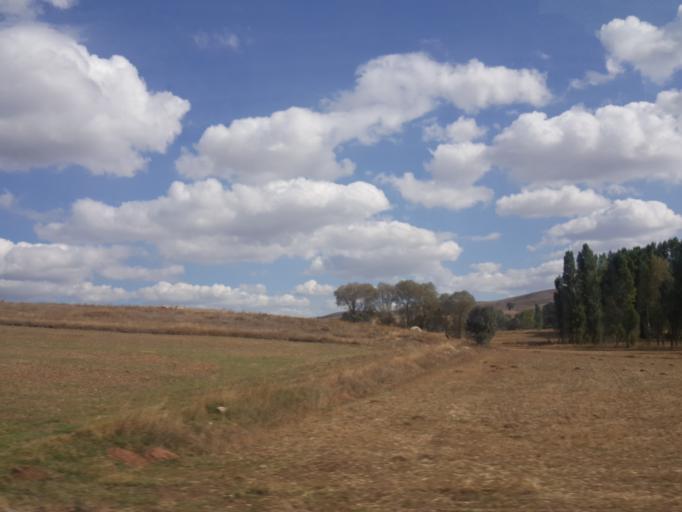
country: TR
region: Tokat
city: Artova
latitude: 40.1451
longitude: 36.3749
